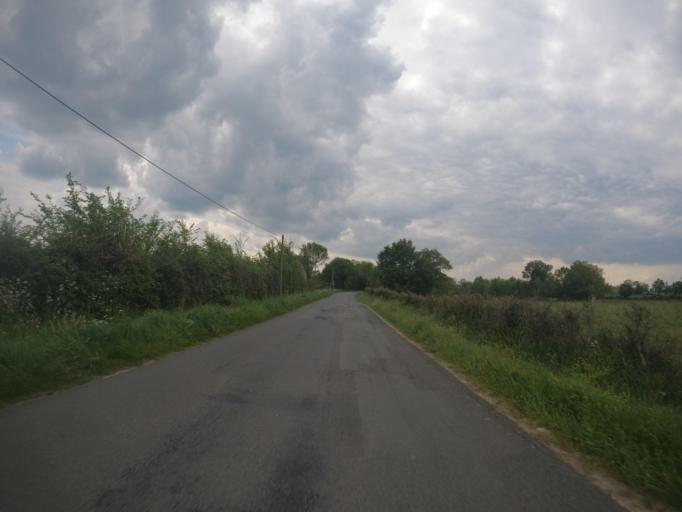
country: FR
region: Poitou-Charentes
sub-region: Departement des Deux-Sevres
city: Chiche
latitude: 46.8573
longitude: -0.3132
